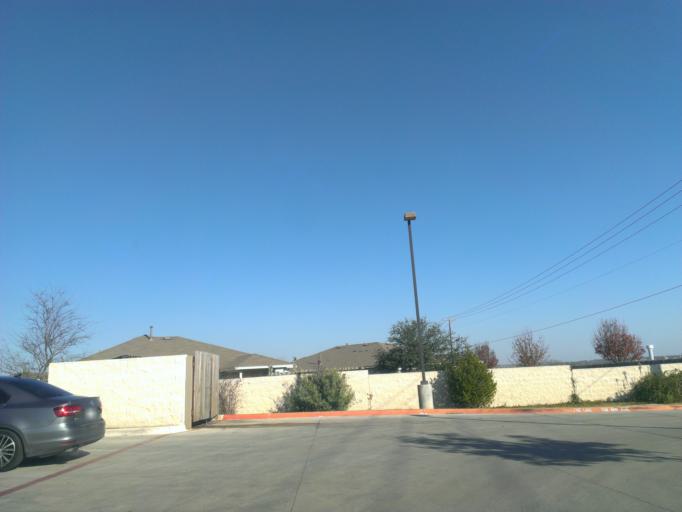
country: US
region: Texas
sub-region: Williamson County
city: Hutto
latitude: 30.5473
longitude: -97.6147
